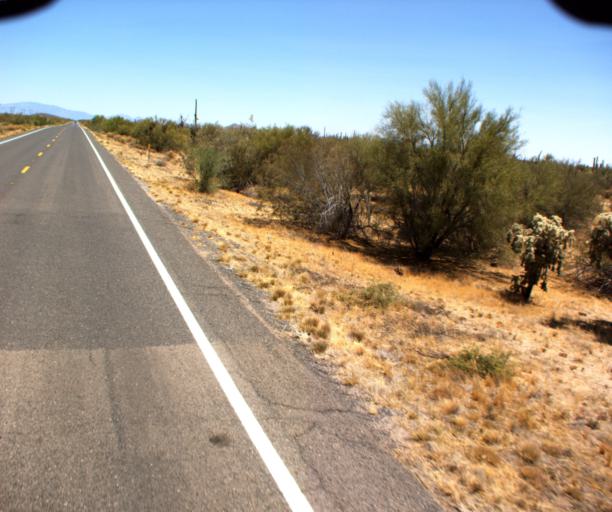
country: US
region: Arizona
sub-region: Pinal County
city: Florence
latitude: 32.8208
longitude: -111.2024
